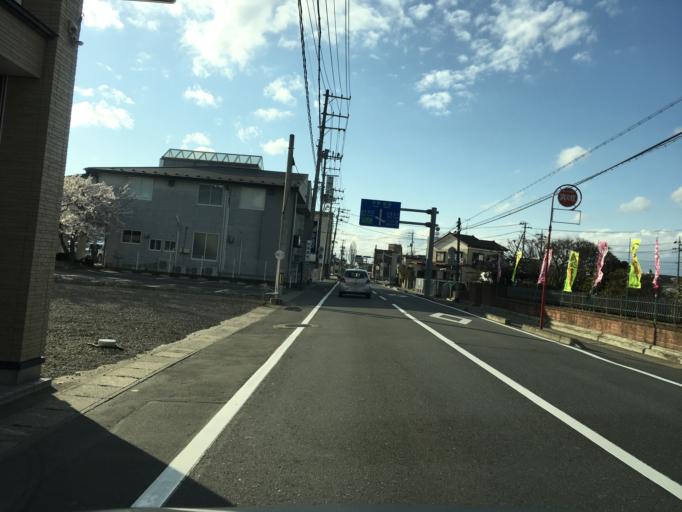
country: JP
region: Miyagi
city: Ishinomaki
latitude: 38.4394
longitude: 141.2918
